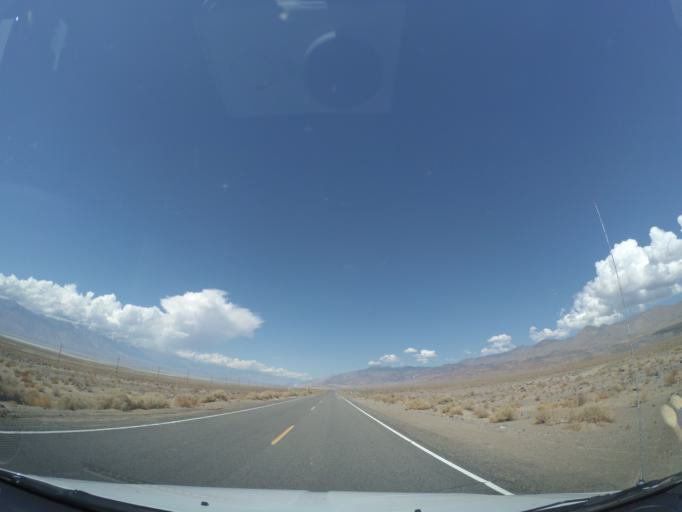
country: US
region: California
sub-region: Inyo County
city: Lone Pine
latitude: 36.4327
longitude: -117.8264
